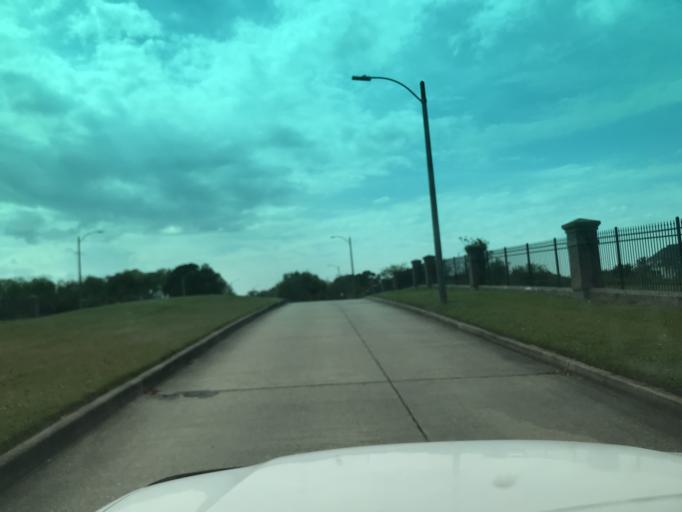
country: US
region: Louisiana
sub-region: Saint Bernard Parish
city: Chalmette
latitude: 30.0397
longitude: -89.9489
